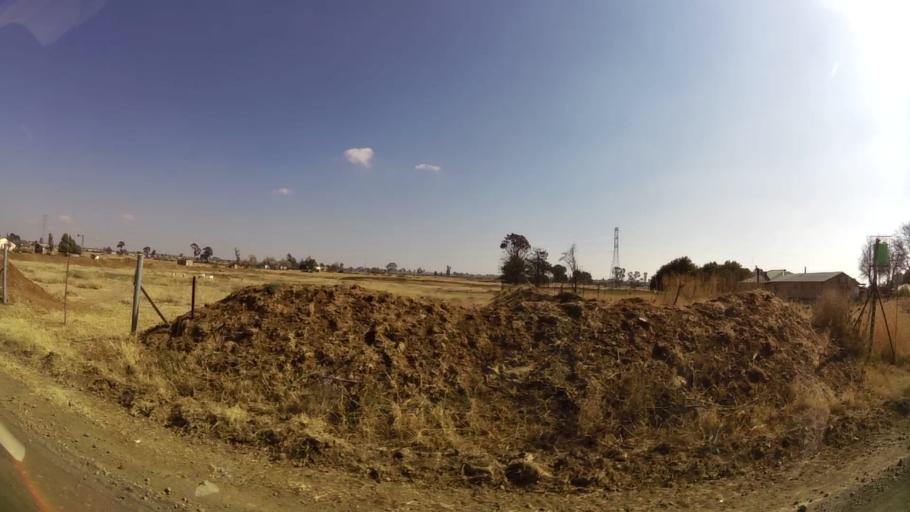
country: ZA
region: Orange Free State
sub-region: Mangaung Metropolitan Municipality
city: Bloemfontein
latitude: -29.1696
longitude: 26.3086
